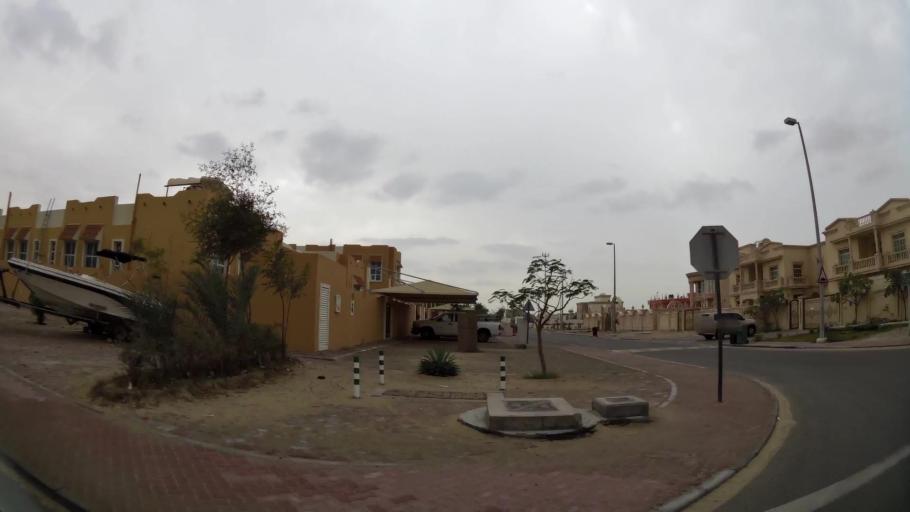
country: AE
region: Abu Dhabi
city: Abu Dhabi
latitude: 24.3734
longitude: 54.6477
